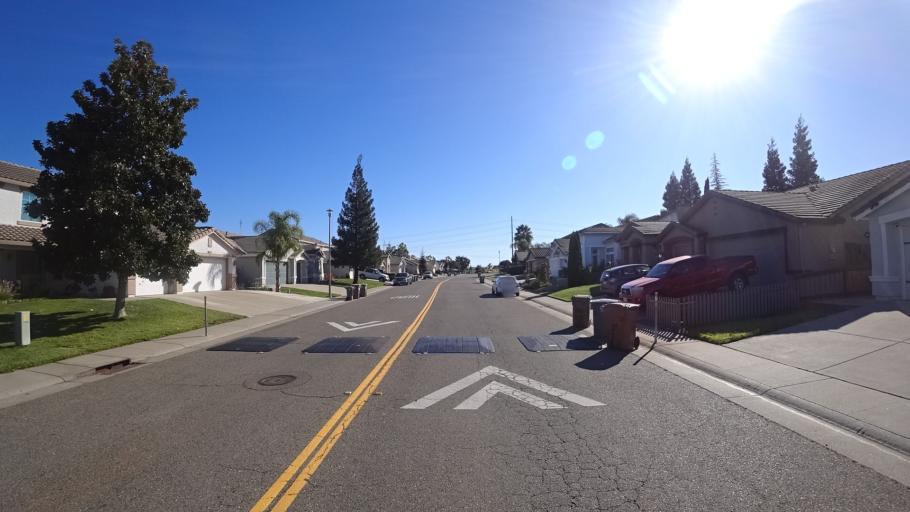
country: US
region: California
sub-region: Sacramento County
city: Vineyard
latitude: 38.4489
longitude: -121.3552
